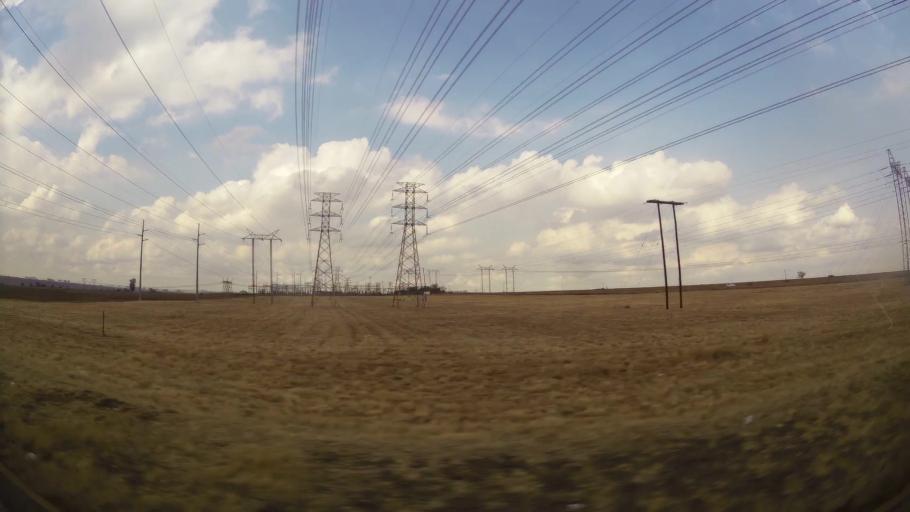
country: ZA
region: Orange Free State
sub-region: Fezile Dabi District Municipality
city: Sasolburg
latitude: -26.8229
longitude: 27.9033
